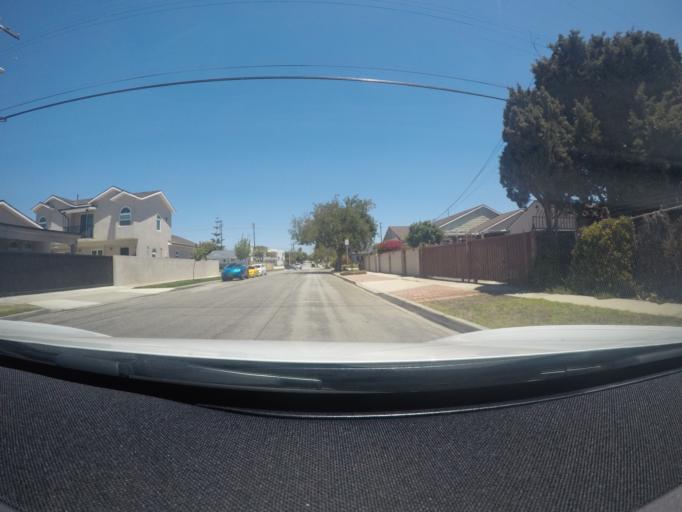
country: US
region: California
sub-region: Los Angeles County
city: Torrance
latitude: 33.8570
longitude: -118.3576
